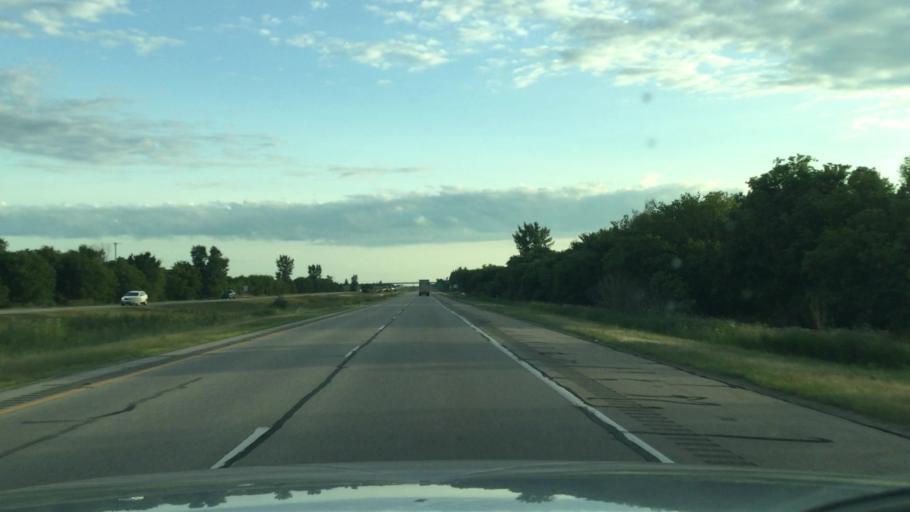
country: US
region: Michigan
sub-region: Clinton County
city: Saint Johns
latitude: 42.9696
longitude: -84.5185
